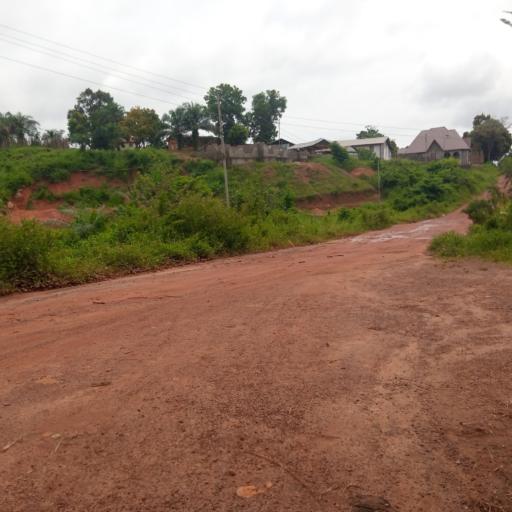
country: SL
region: Eastern Province
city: Kenema
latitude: 7.8883
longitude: -11.1938
